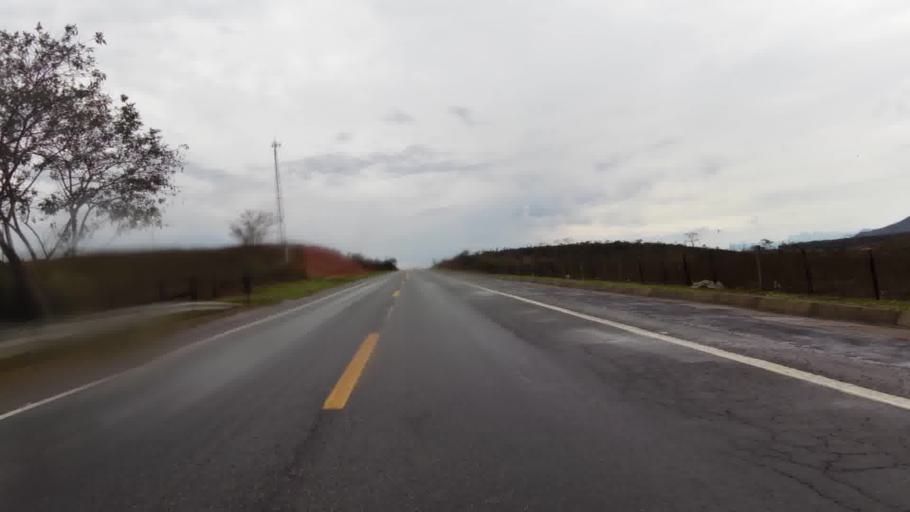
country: BR
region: Rio de Janeiro
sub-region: Campos Dos Goytacazes
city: Campos
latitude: -21.4839
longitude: -41.3399
